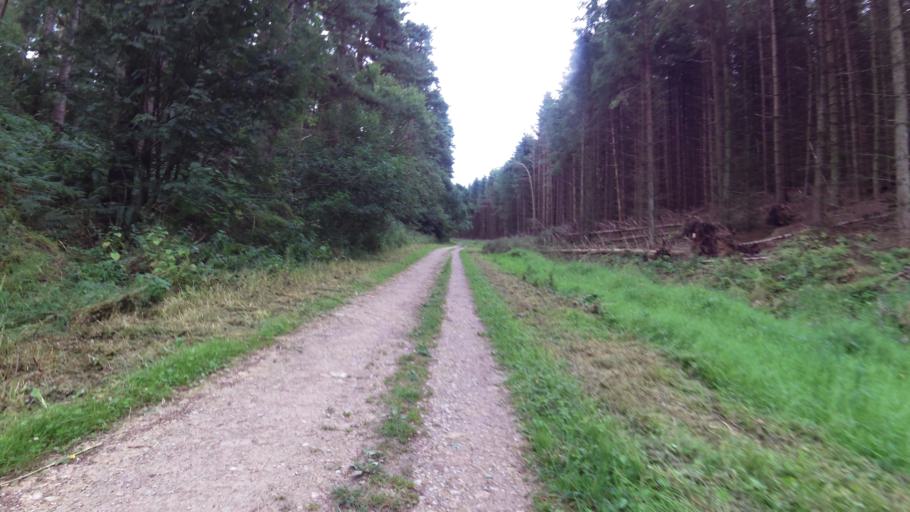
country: GB
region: England
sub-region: North Yorkshire
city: Thornton Dale
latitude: 54.2840
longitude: -0.6763
